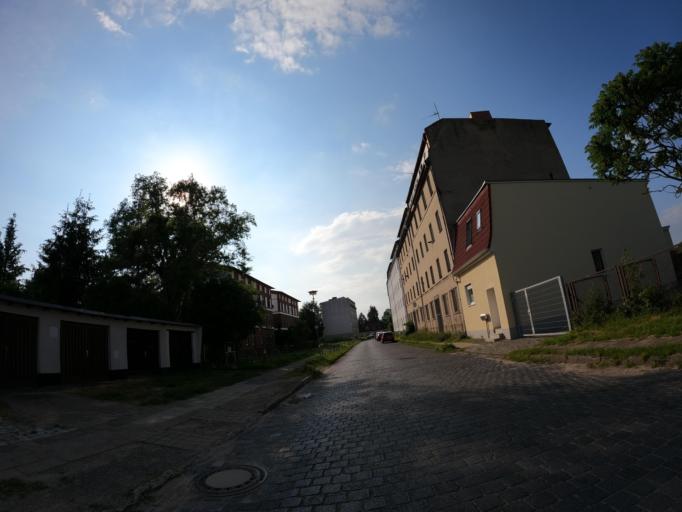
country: DE
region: Mecklenburg-Vorpommern
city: Stralsund
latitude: 54.3053
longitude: 13.0758
